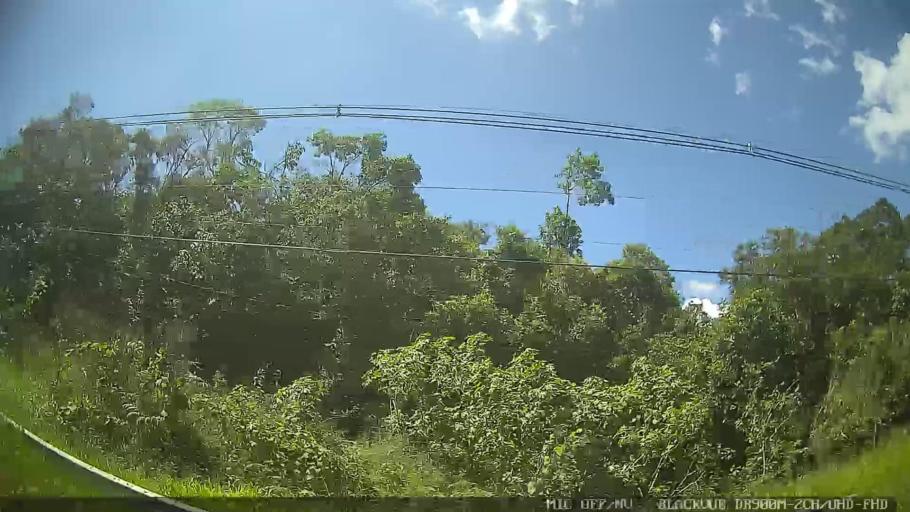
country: BR
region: Sao Paulo
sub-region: Mogi das Cruzes
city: Mogi das Cruzes
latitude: -23.6087
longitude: -46.1691
